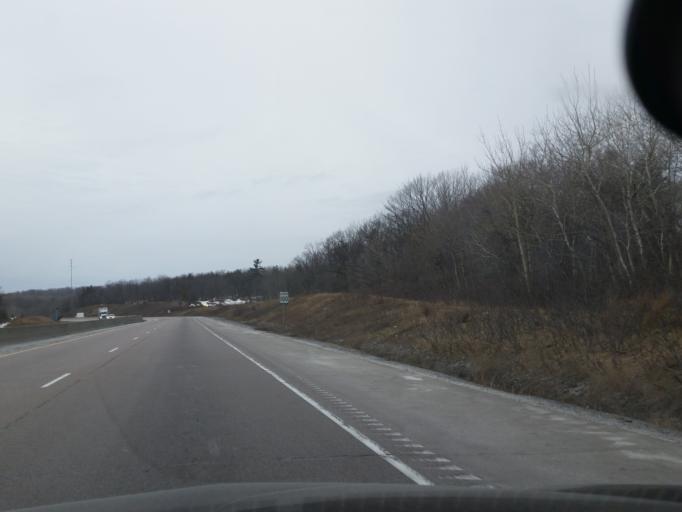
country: CA
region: Ontario
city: Quinte West
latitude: 44.1180
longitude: -77.6371
